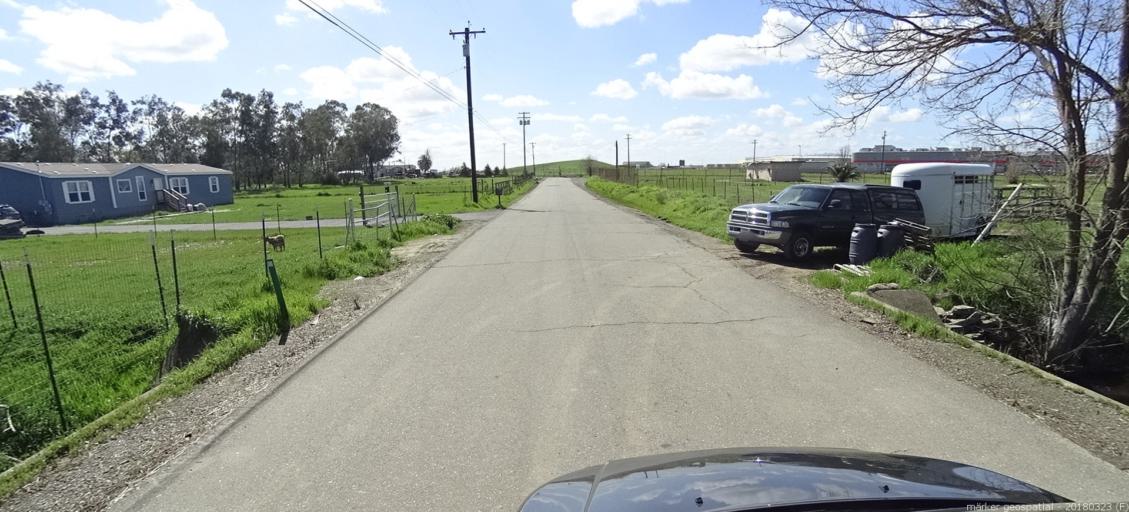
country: US
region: California
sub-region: Sacramento County
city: North Highlands
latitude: 38.6732
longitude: -121.4107
